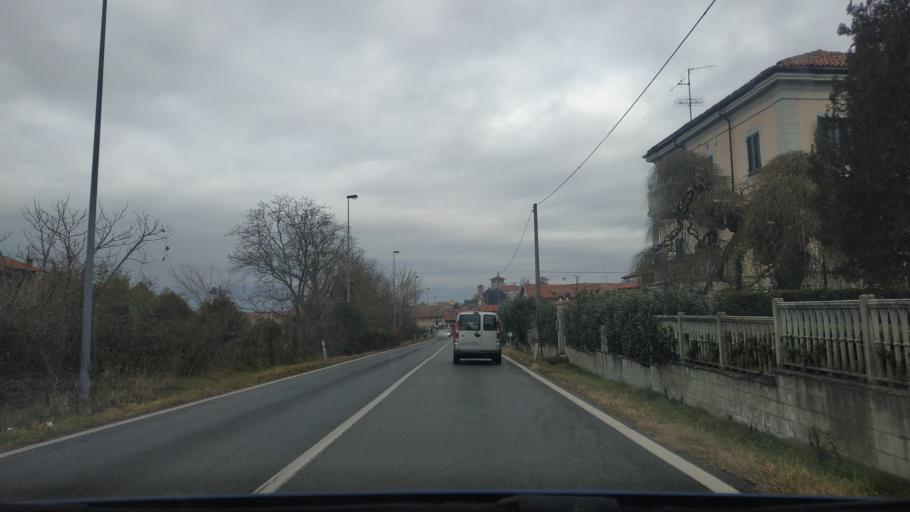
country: IT
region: Piedmont
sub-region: Provincia di Torino
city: Mercenasco
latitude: 45.3510
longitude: 7.8830
